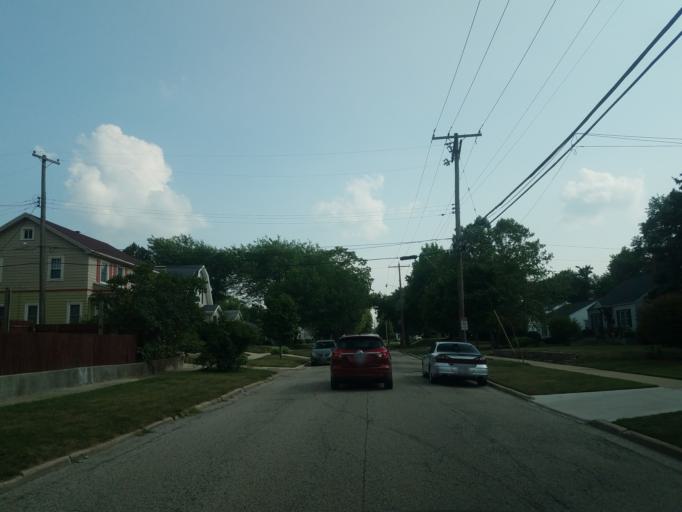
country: US
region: Illinois
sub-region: McLean County
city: Bloomington
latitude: 40.4738
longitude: -88.9724
